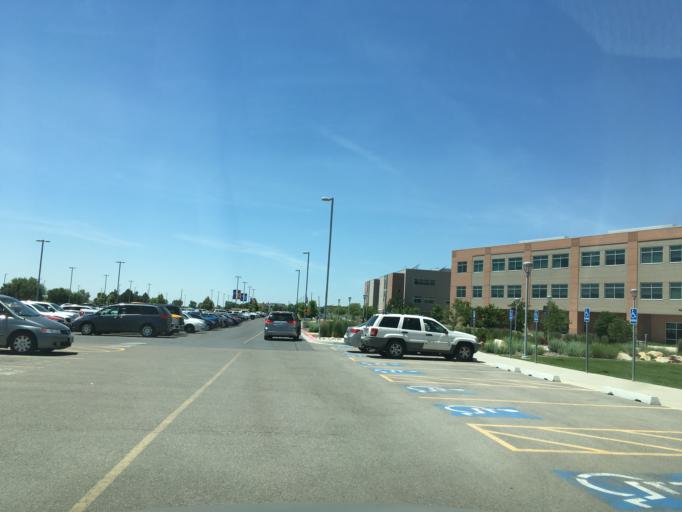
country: US
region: Utah
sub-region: Davis County
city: Hill Air Force Bace
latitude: 41.0982
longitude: -111.9820
